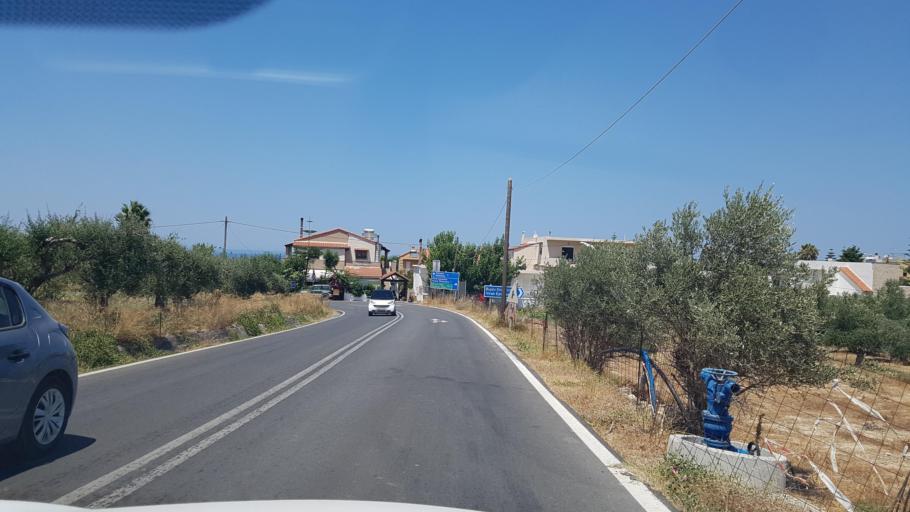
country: GR
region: Crete
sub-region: Nomos Rethymnis
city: Agia Foteini
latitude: 35.3551
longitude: 24.5893
